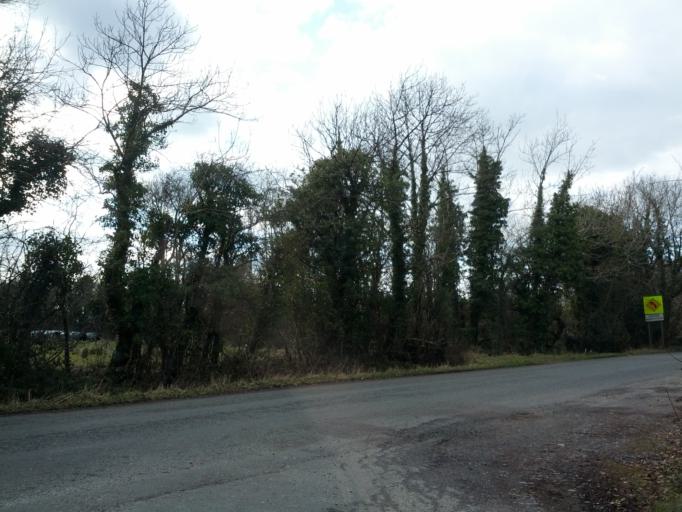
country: IE
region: Connaught
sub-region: County Galway
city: Athenry
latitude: 53.4349
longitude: -8.6748
